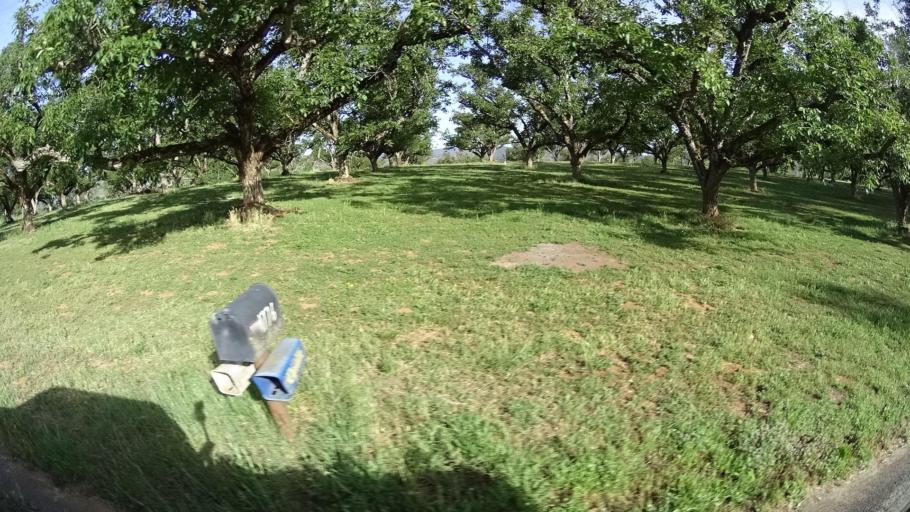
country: US
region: California
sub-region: Lake County
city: Lakeport
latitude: 39.0587
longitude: -122.9373
